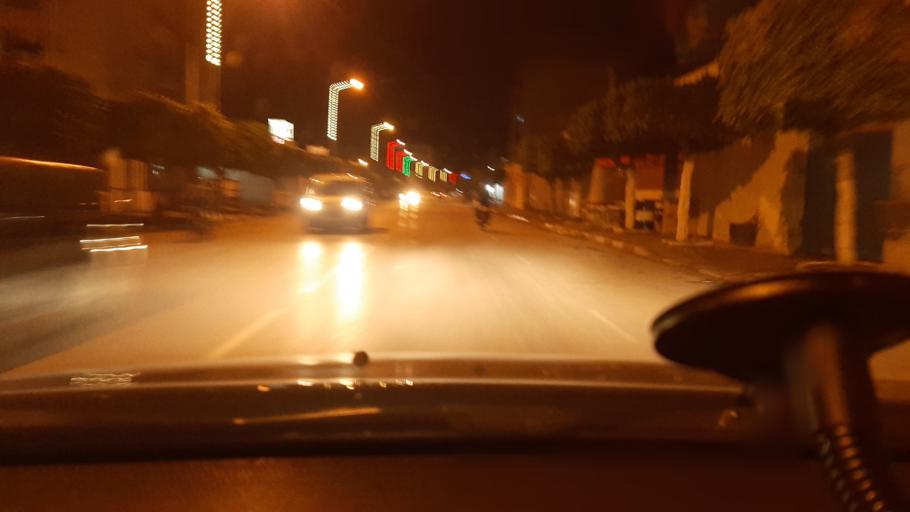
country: TN
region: Safaqis
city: Sfax
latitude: 34.7852
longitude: 10.7211
